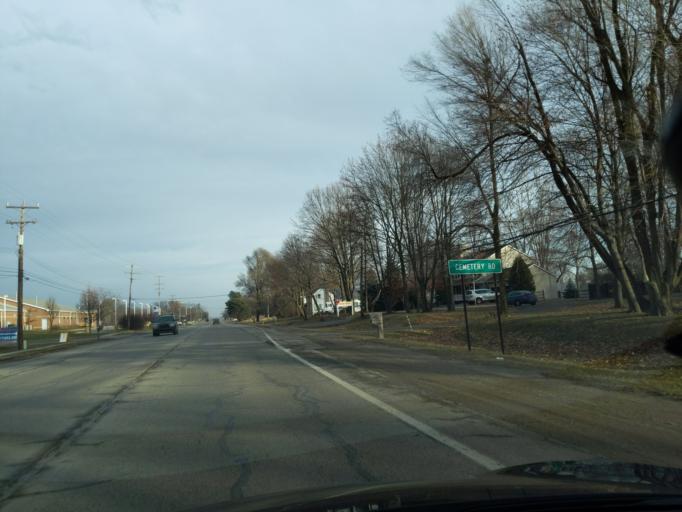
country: US
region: Michigan
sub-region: Livingston County
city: Fowlerville
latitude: 42.6608
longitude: -84.0562
